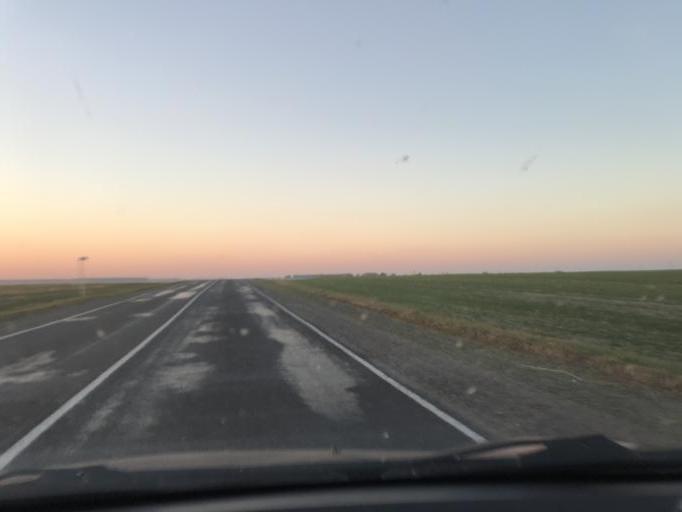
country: BY
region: Gomel
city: Horad Rechytsa
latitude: 52.1733
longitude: 30.5711
